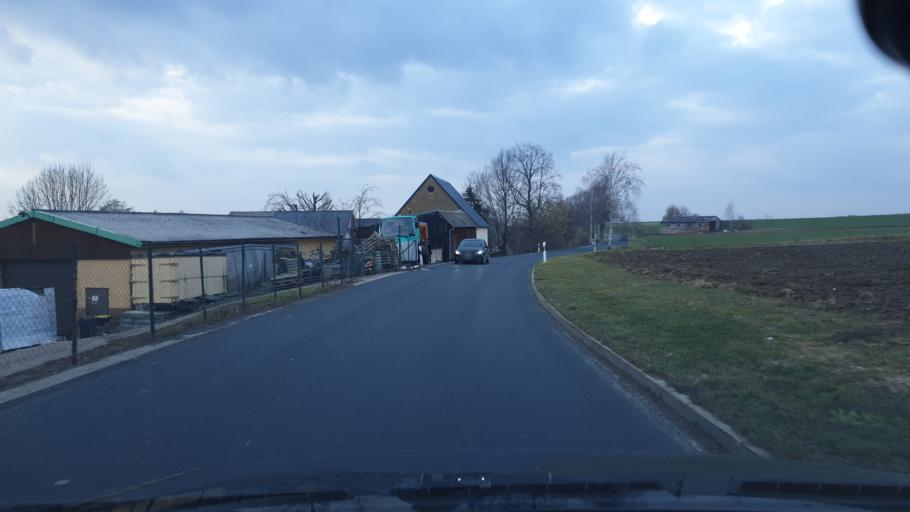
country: DE
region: Saxony
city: Erlau
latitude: 50.9881
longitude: 12.9303
